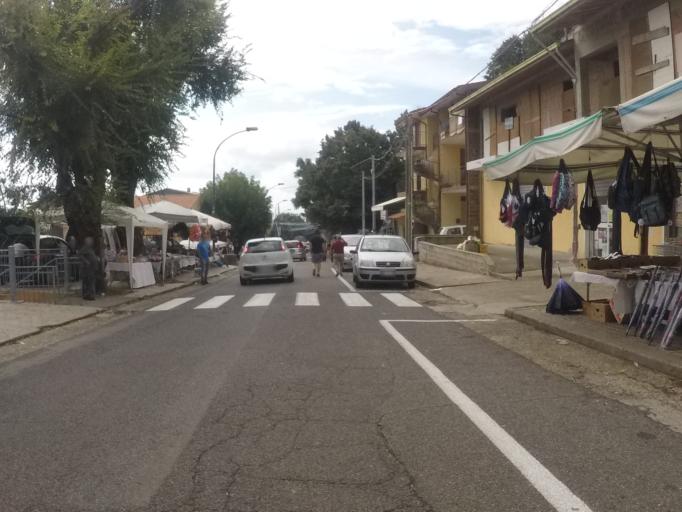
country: IT
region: Sardinia
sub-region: Provincia di Oristano
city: Bonarcado
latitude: 40.1013
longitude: 8.6544
